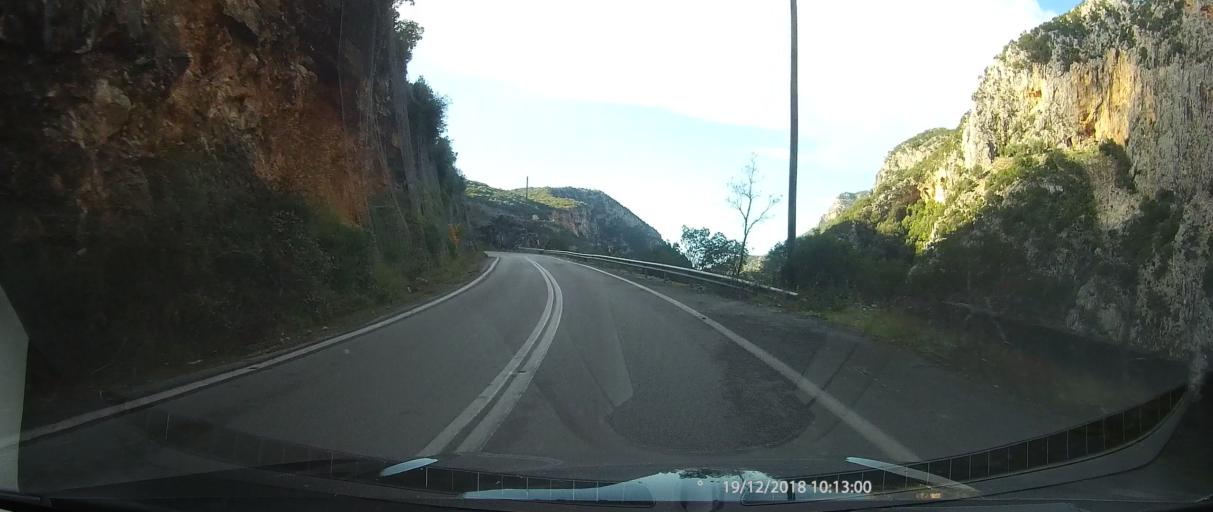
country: GR
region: Peloponnese
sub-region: Nomos Messinias
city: Kalamata
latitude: 37.0879
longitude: 22.1624
